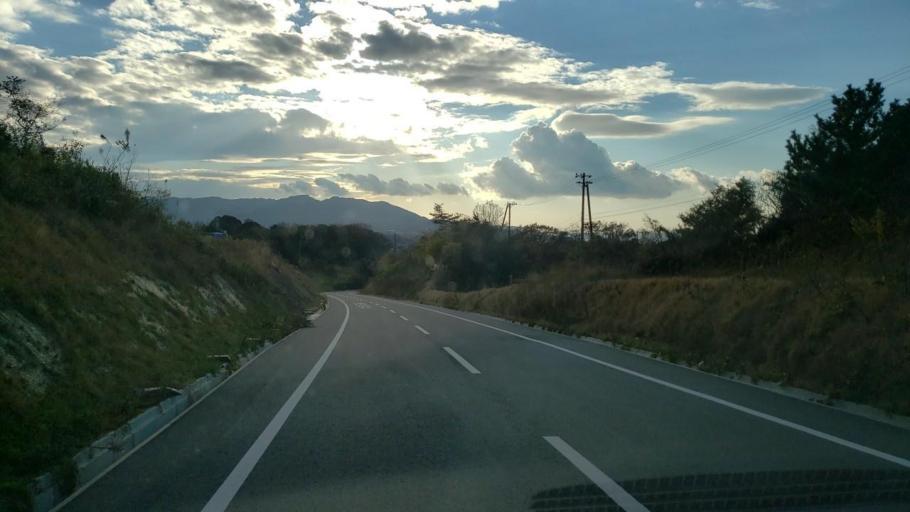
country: JP
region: Hyogo
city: Akashi
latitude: 34.5490
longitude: 134.9757
